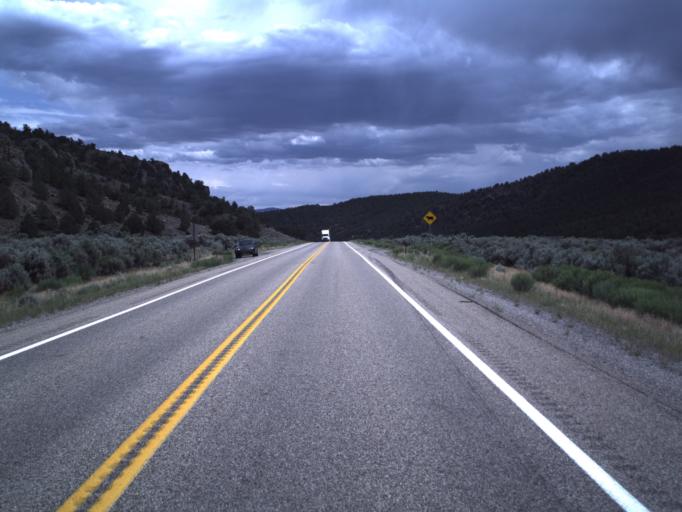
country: US
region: Utah
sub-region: Garfield County
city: Panguitch
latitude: 37.9820
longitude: -112.4865
